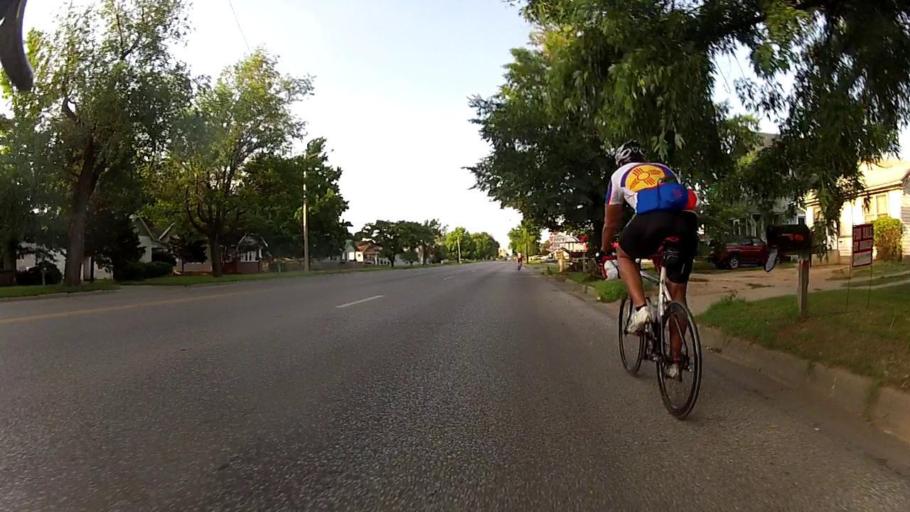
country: US
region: Kansas
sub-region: Cowley County
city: Arkansas City
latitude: 37.0743
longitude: -97.0392
